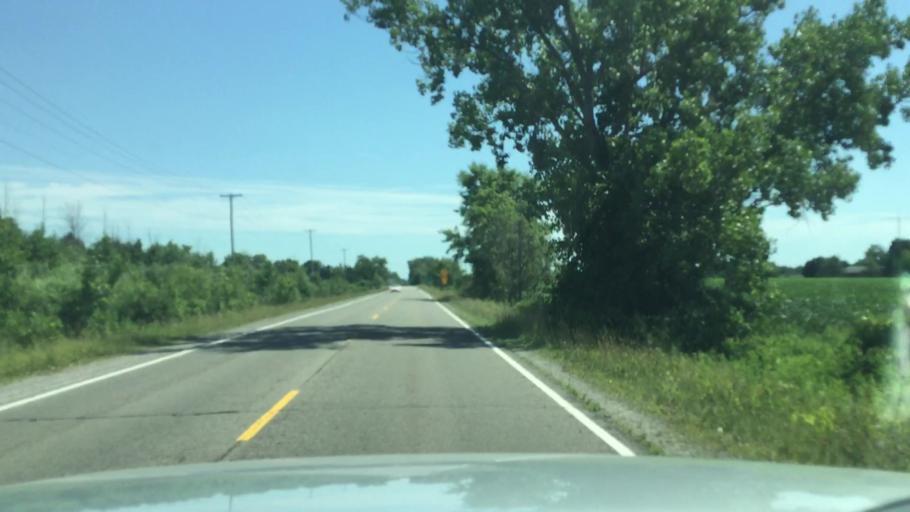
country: US
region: Michigan
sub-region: Genesee County
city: Swartz Creek
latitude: 42.9462
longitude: -83.8109
